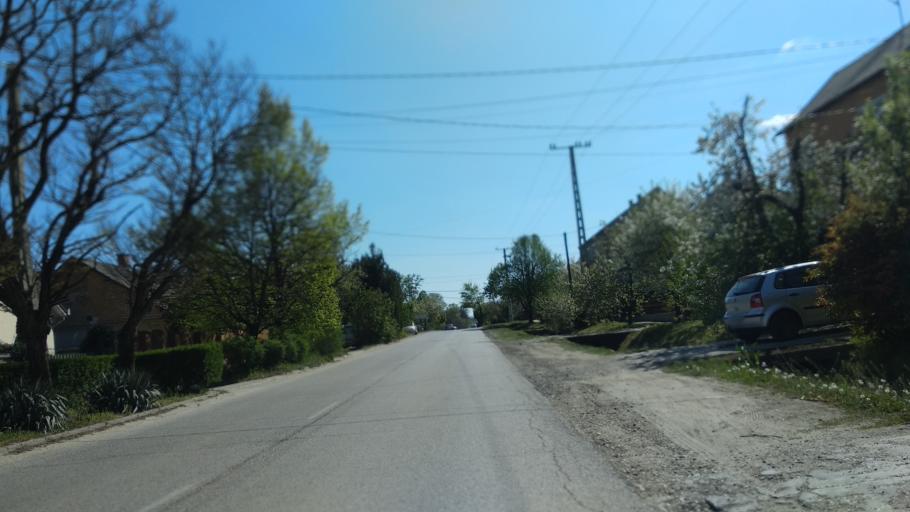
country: HU
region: Pest
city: Godollo
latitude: 47.5891
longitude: 19.3446
